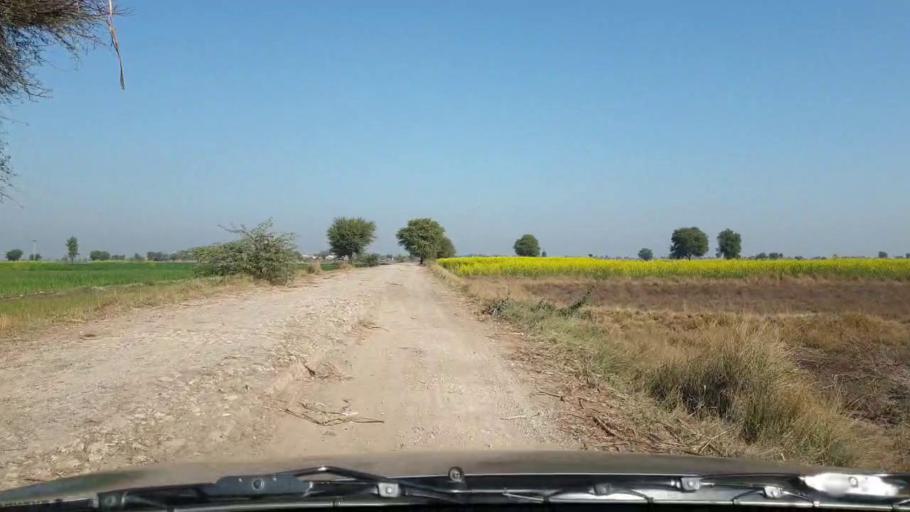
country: PK
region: Sindh
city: Jhol
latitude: 25.9596
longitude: 68.8227
